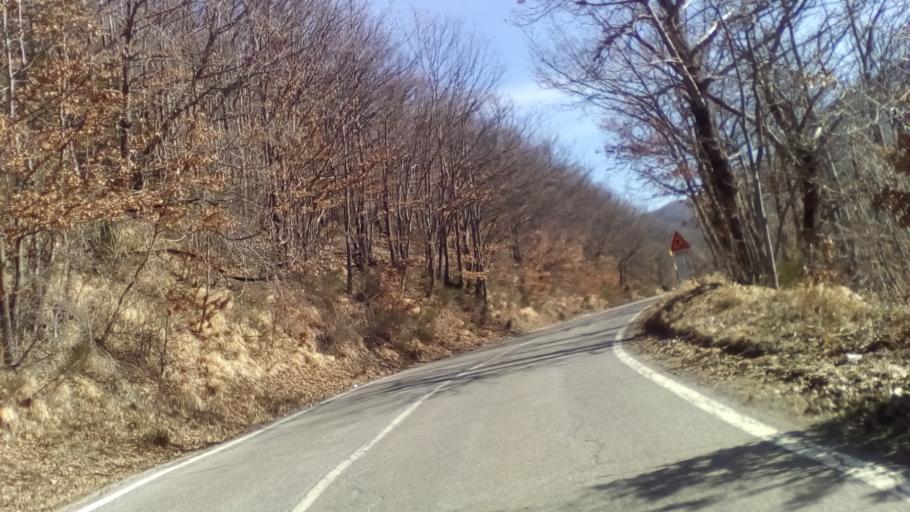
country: IT
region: Emilia-Romagna
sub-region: Provincia di Modena
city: Pievepelago
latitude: 44.2152
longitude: 10.6213
